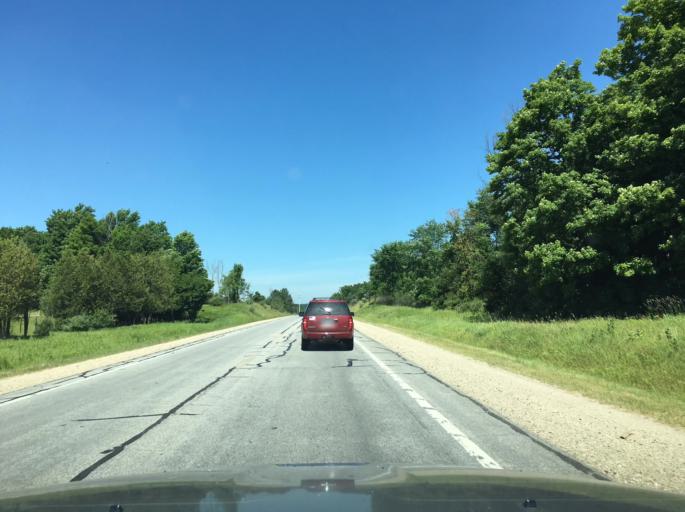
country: US
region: Michigan
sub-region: Osceola County
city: Reed City
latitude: 43.8764
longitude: -85.4967
